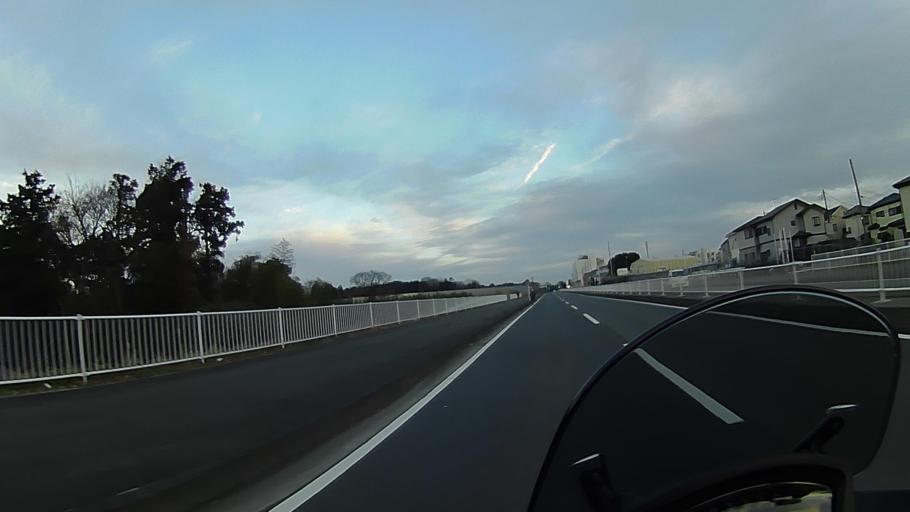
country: JP
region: Kanagawa
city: Atsugi
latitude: 35.4047
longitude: 139.4203
